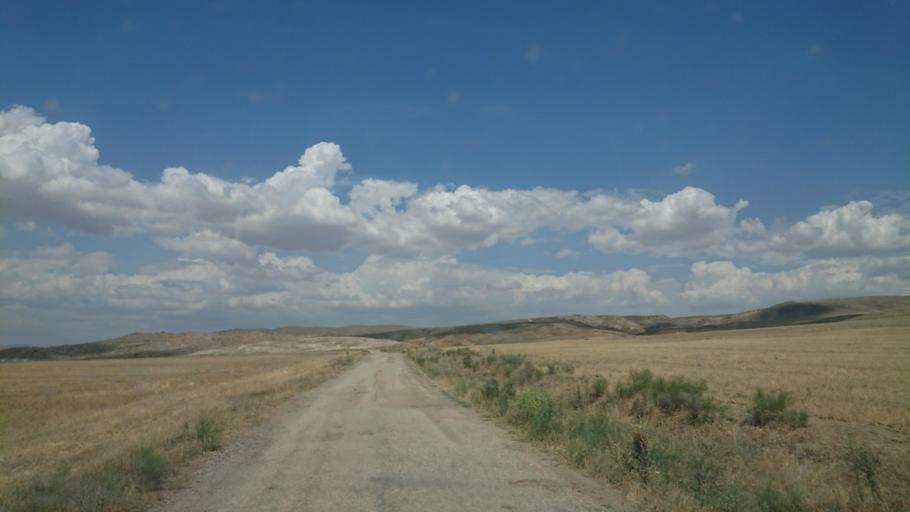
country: TR
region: Aksaray
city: Sariyahsi
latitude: 38.9916
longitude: 33.9115
